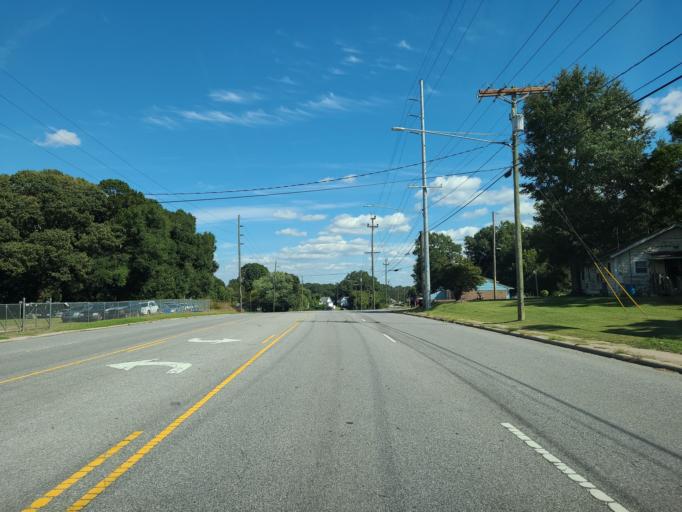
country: US
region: North Carolina
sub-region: Gaston County
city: Gastonia
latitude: 35.2573
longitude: -81.2050
